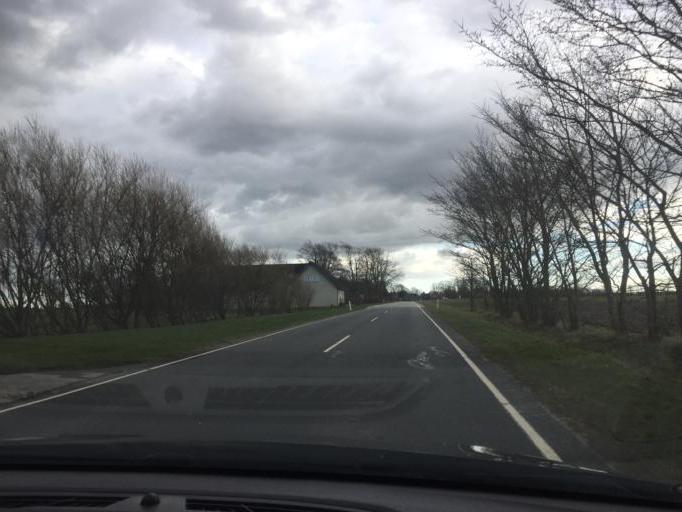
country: DK
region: South Denmark
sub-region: Kerteminde Kommune
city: Langeskov
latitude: 55.2865
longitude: 10.6094
